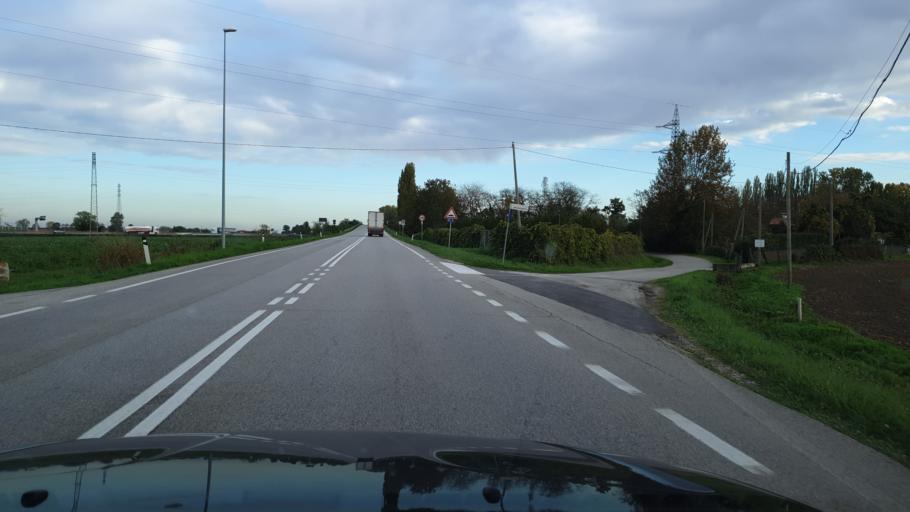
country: IT
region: Veneto
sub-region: Provincia di Padova
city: Monselice
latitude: 45.2367
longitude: 11.7702
